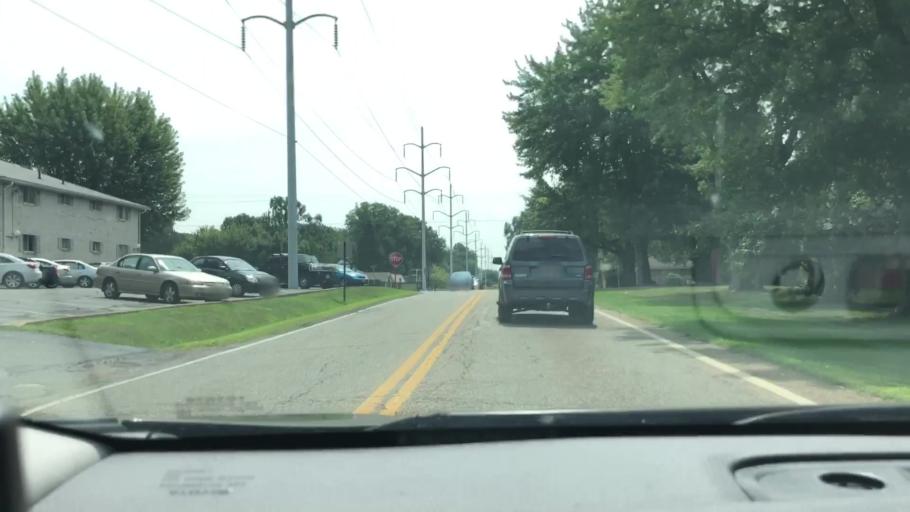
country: US
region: Ohio
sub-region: Stark County
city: Perry Heights
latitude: 40.8223
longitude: -81.4346
